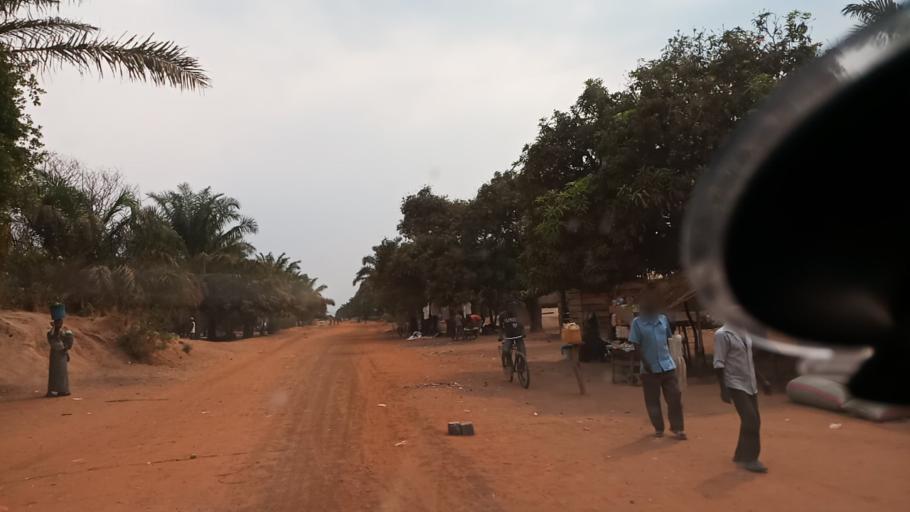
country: ZM
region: Luapula
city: Nchelenge
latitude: -9.1306
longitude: 28.3007
